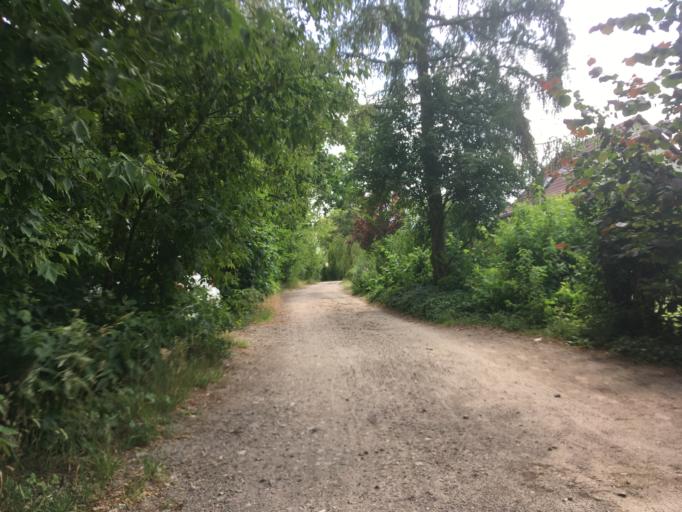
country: DE
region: Berlin
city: Lichterfelde
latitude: 52.3971
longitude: 13.3115
